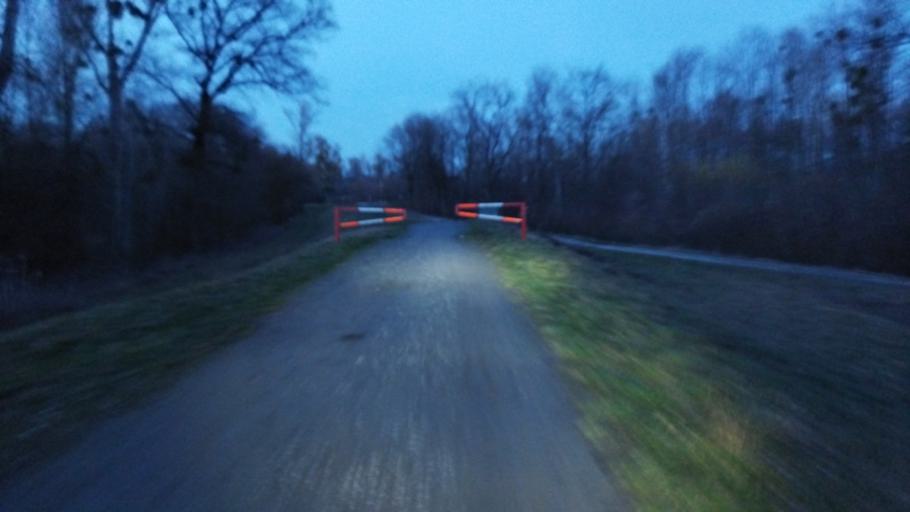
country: DE
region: Baden-Wuerttemberg
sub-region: Karlsruhe Region
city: Eggenstein-Leopoldshafen
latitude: 49.0977
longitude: 8.3757
